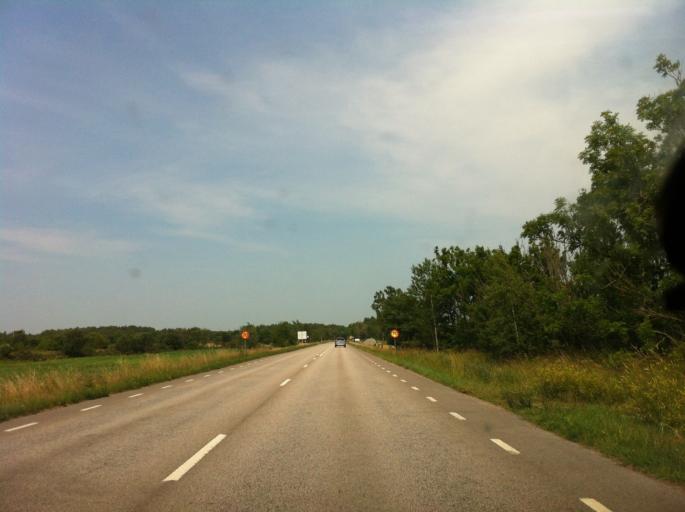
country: SE
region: Kalmar
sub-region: Borgholms Kommun
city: Borgholm
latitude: 57.0118
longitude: 16.8466
